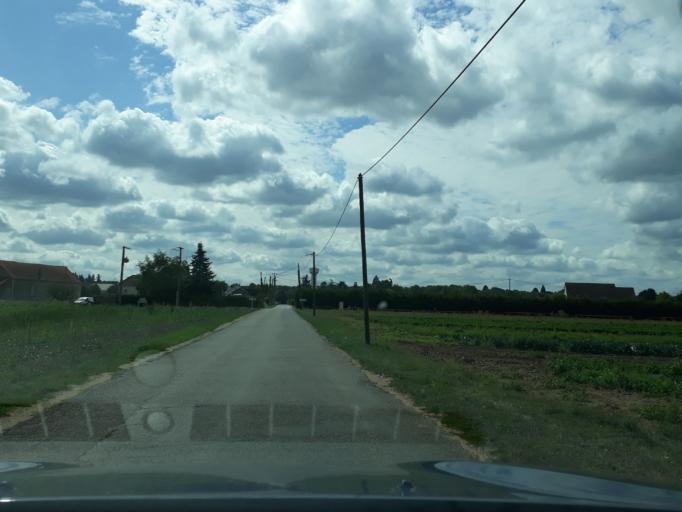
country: FR
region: Centre
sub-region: Departement du Loiret
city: Saint-Cyr-en-Val
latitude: 47.8396
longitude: 1.9697
